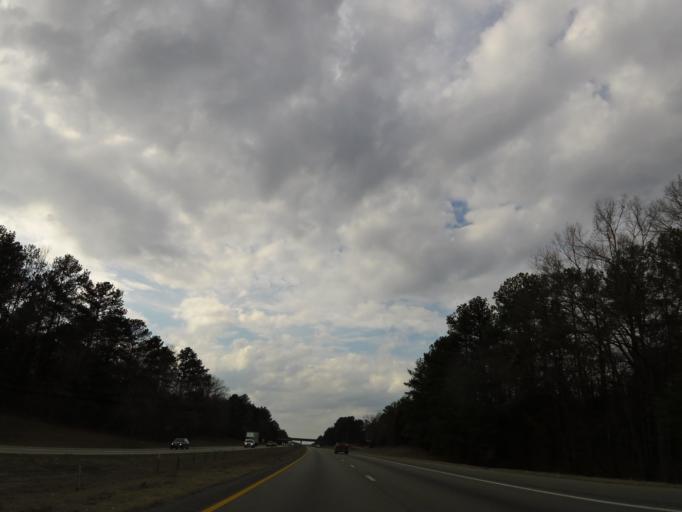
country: US
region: South Carolina
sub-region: Richland County
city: Lake Murray of Richland
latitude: 34.1345
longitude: -81.2125
